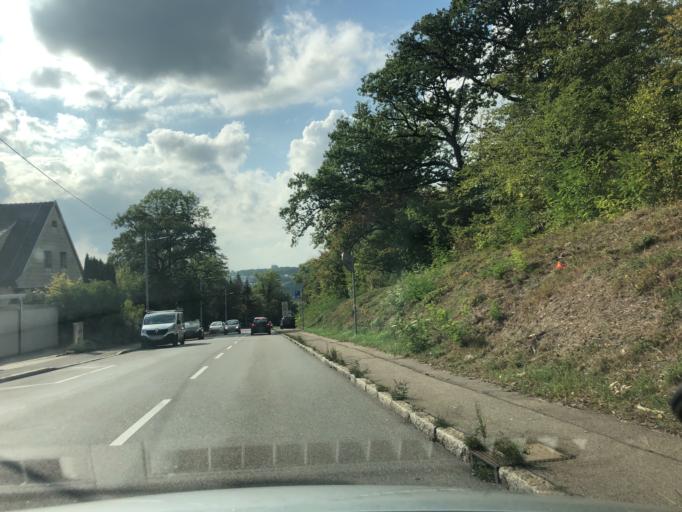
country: DE
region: Baden-Wuerttemberg
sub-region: Regierungsbezirk Stuttgart
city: Stuttgart
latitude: 48.7494
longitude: 9.1534
